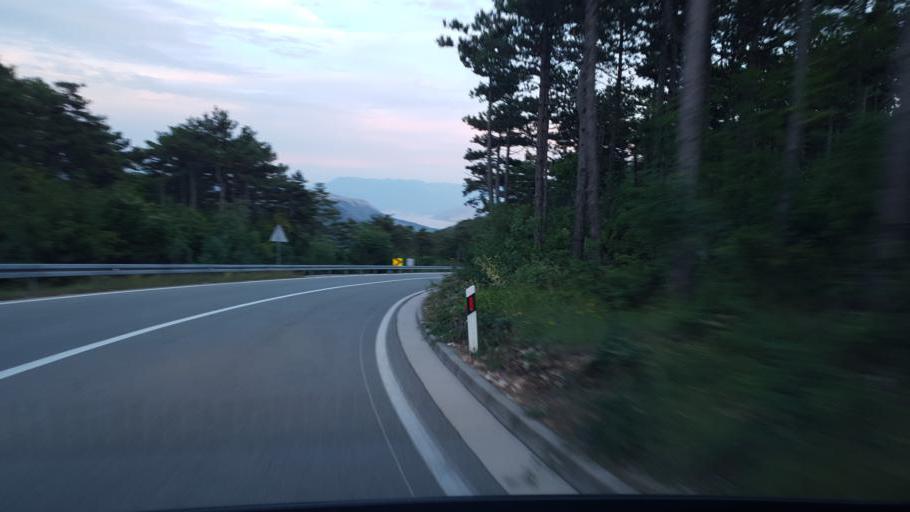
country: HR
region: Primorsko-Goranska
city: Punat
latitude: 45.0299
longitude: 14.6730
